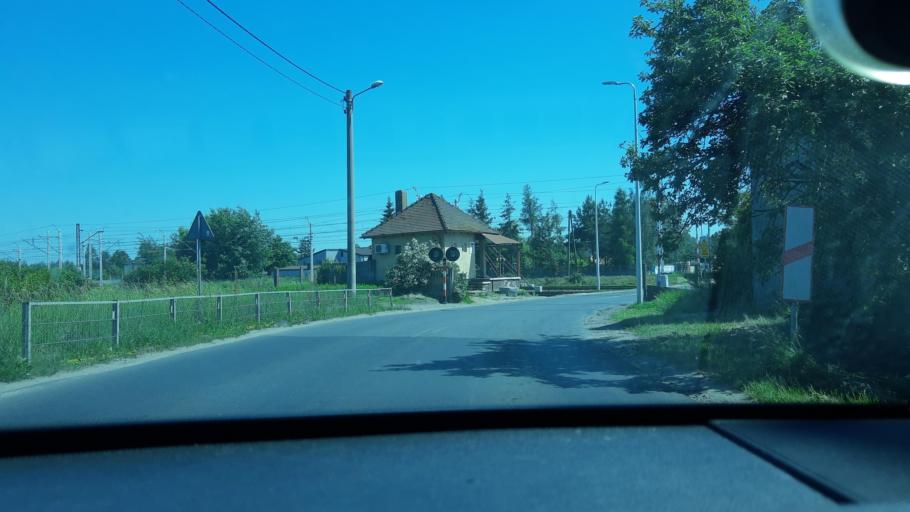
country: PL
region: Lodz Voivodeship
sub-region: Powiat zdunskowolski
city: Zdunska Wola
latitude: 51.6126
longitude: 18.9652
